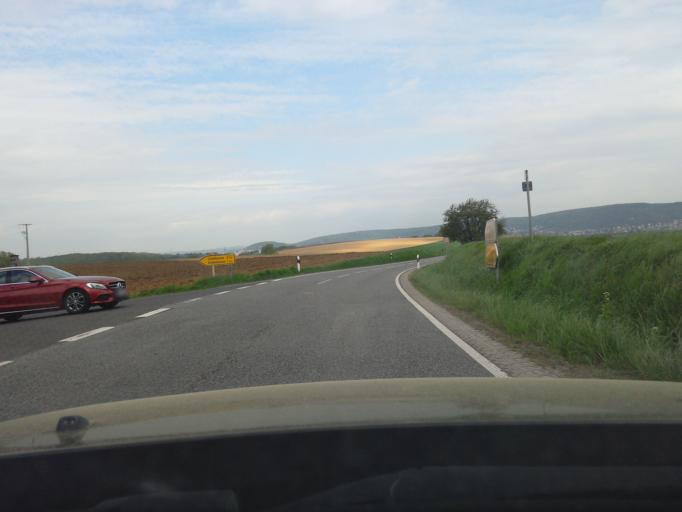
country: DE
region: Hesse
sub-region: Regierungsbezirk Darmstadt
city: Gelnhausen
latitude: 50.1639
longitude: 9.2037
